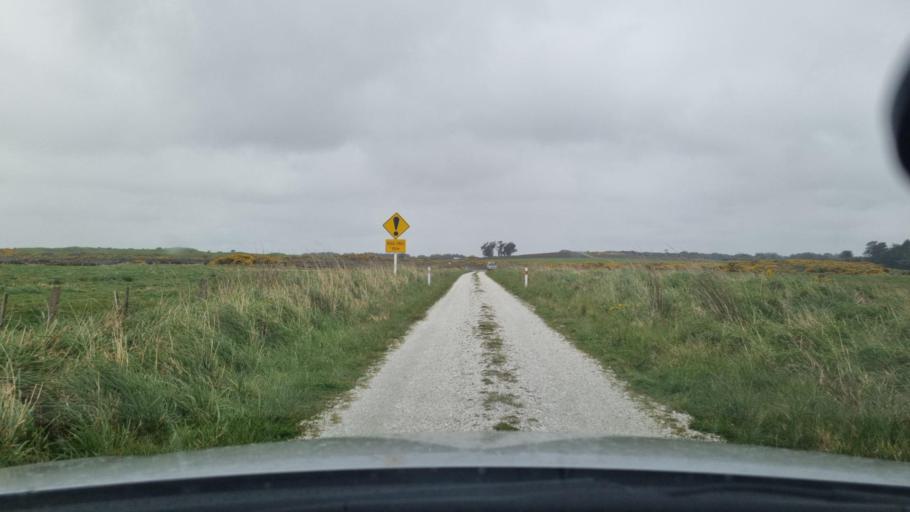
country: NZ
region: Southland
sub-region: Invercargill City
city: Bluff
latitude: -46.5202
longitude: 168.2802
